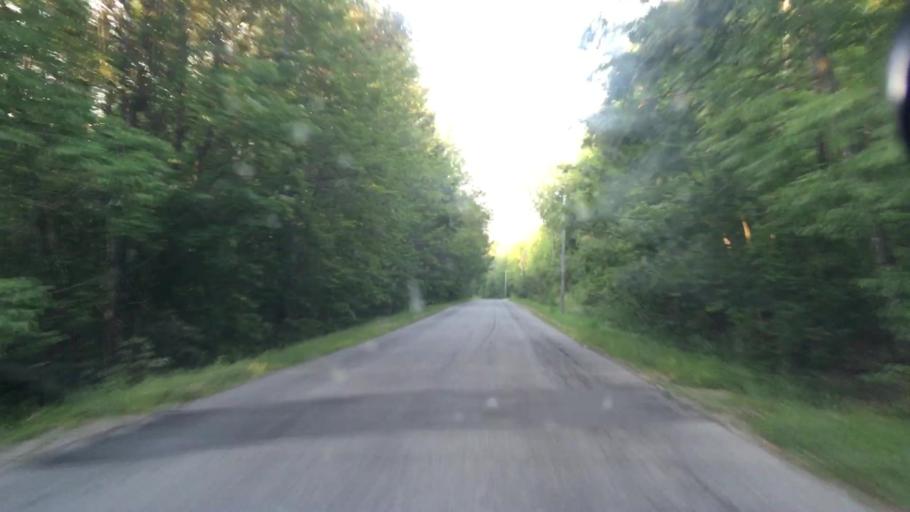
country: US
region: Maine
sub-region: Waldo County
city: Frankfort
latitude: 44.6672
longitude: -68.9260
